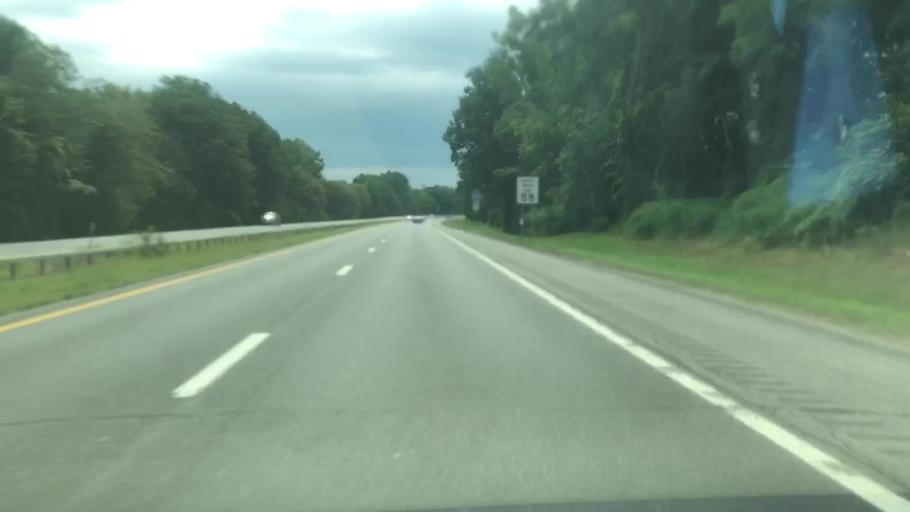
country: US
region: New York
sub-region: Schenectady County
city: Rotterdam
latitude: 42.7661
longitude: -73.9282
